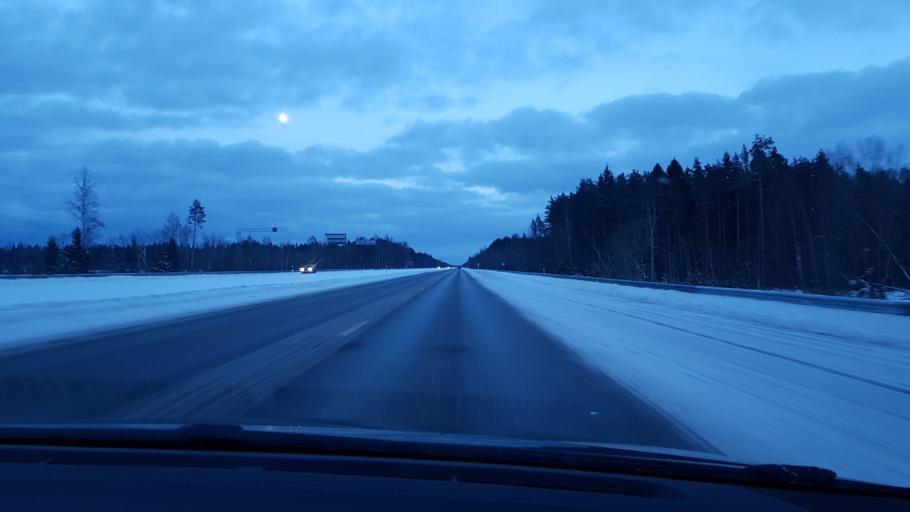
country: EE
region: Harju
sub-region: Kuusalu vald
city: Kuusalu
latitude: 59.4564
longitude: 25.5249
